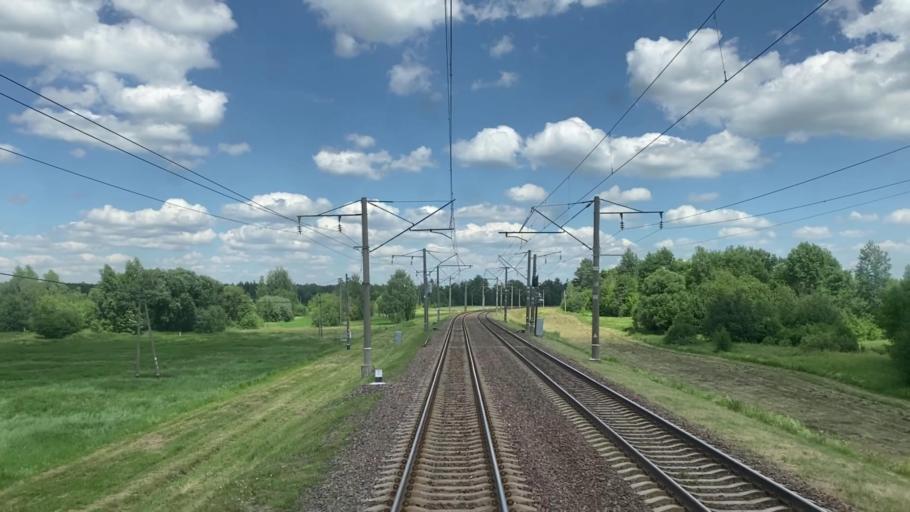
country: BY
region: Brest
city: Ivatsevichy
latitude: 52.7239
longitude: 25.3583
